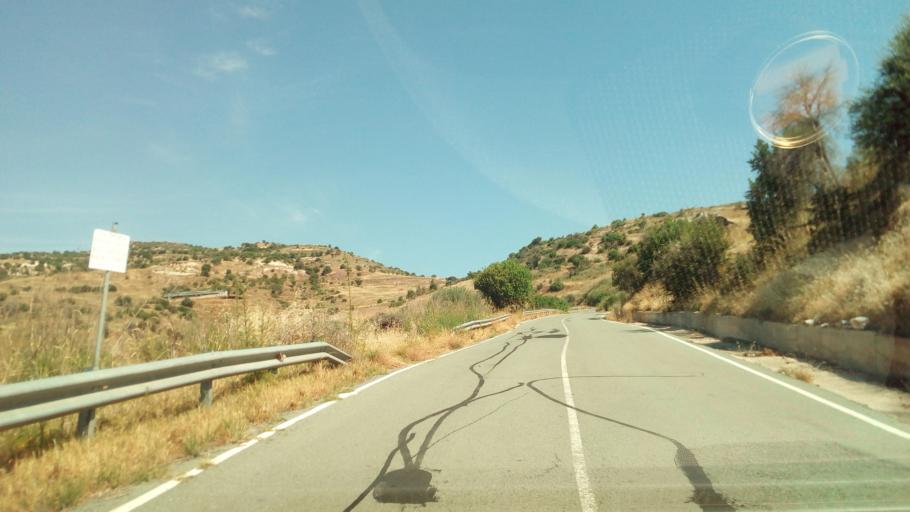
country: CY
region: Limassol
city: Pachna
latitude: 34.7971
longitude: 32.6880
